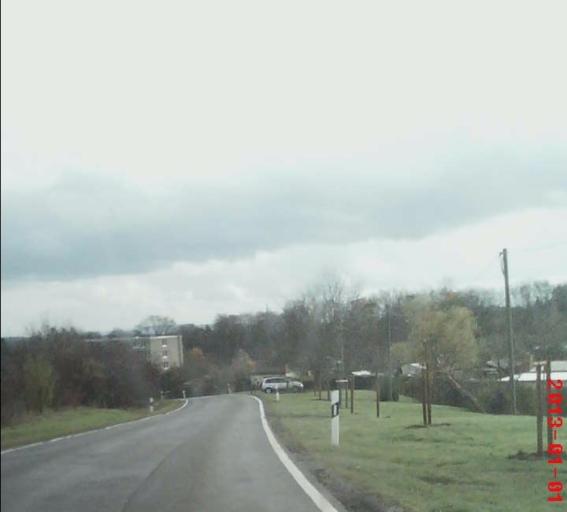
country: DE
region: Thuringia
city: Muehlhausen
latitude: 51.2268
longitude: 10.4264
